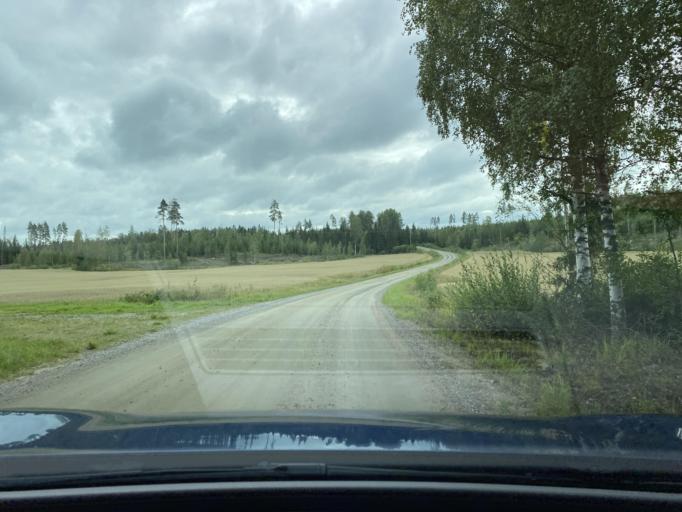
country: FI
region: Pirkanmaa
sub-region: Lounais-Pirkanmaa
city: Punkalaidun
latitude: 61.2154
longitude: 23.1690
